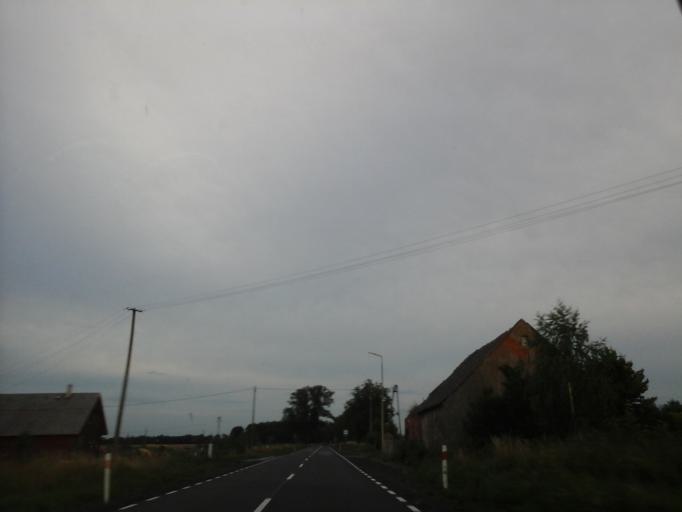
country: PL
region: West Pomeranian Voivodeship
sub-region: Powiat stargardzki
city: Stara Dabrowa
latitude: 53.4256
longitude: 15.0830
